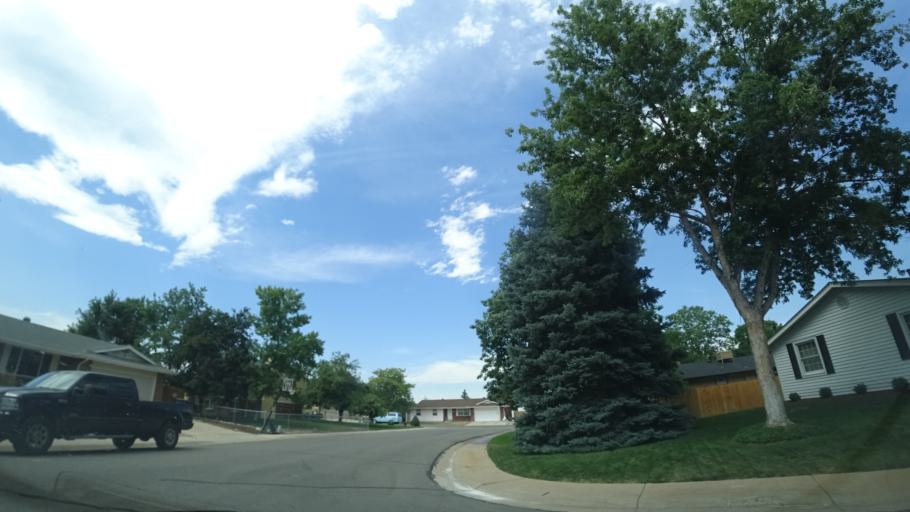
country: US
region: Colorado
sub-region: Jefferson County
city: Lakewood
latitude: 39.6917
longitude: -105.1017
